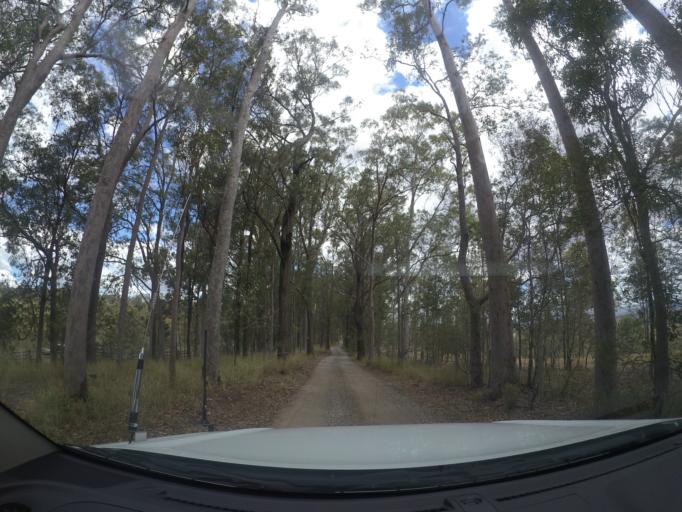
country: AU
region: Queensland
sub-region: Logan
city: Cedar Vale
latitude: -27.9105
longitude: 153.0314
